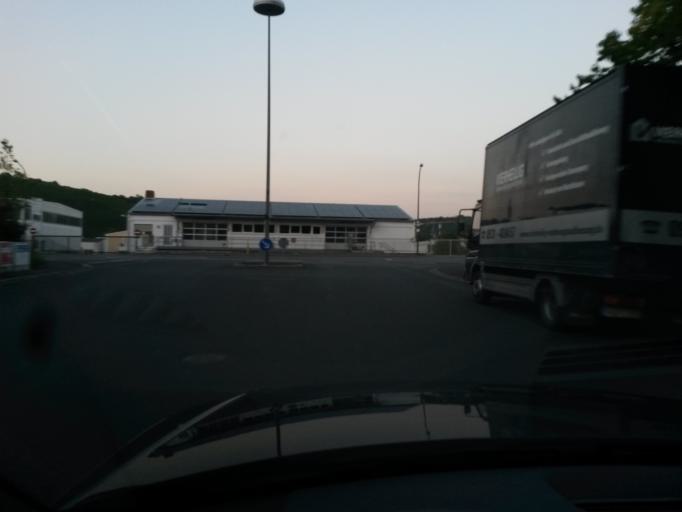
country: DE
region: Bavaria
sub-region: Regierungsbezirk Unterfranken
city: Randersacker
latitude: 49.7562
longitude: 9.9731
